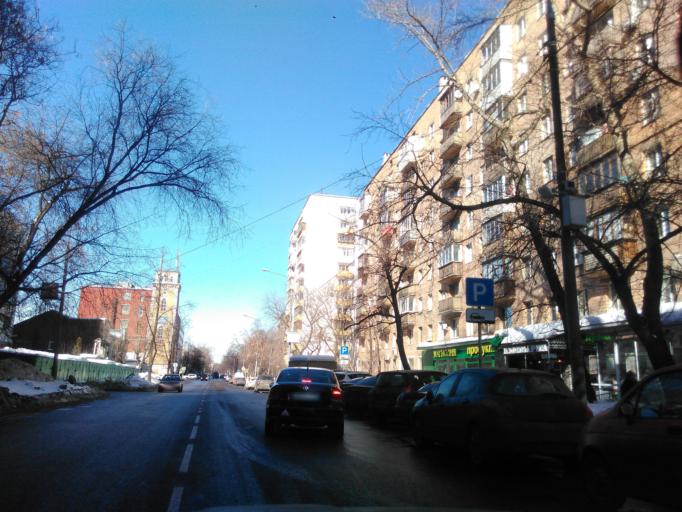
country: RU
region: Moskovskaya
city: Dorogomilovo
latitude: 55.7987
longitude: 37.5675
